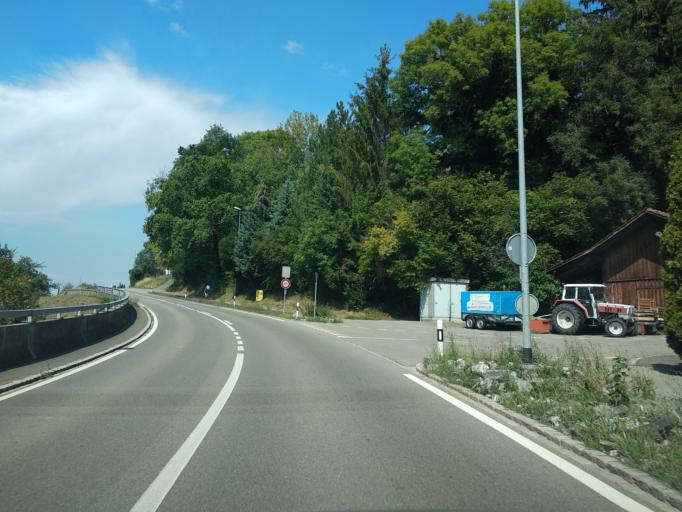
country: CH
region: Zurich
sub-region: Bezirk Winterthur
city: Sulz
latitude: 47.5857
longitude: 8.8156
